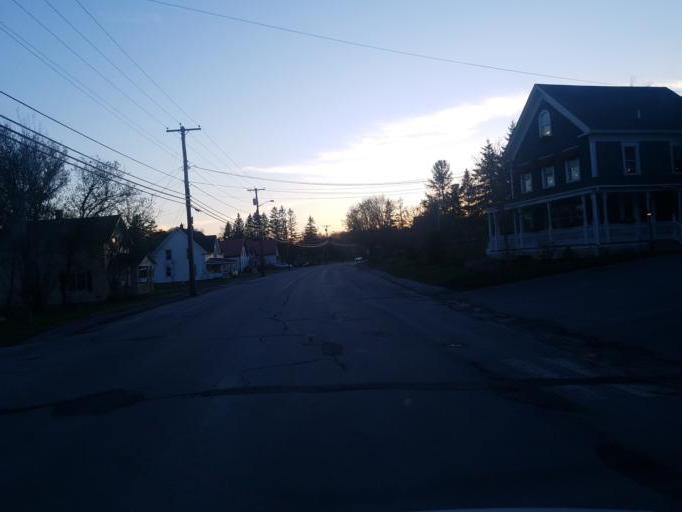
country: US
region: Maine
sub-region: Aroostook County
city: Caribou
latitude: 46.8597
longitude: -68.0218
